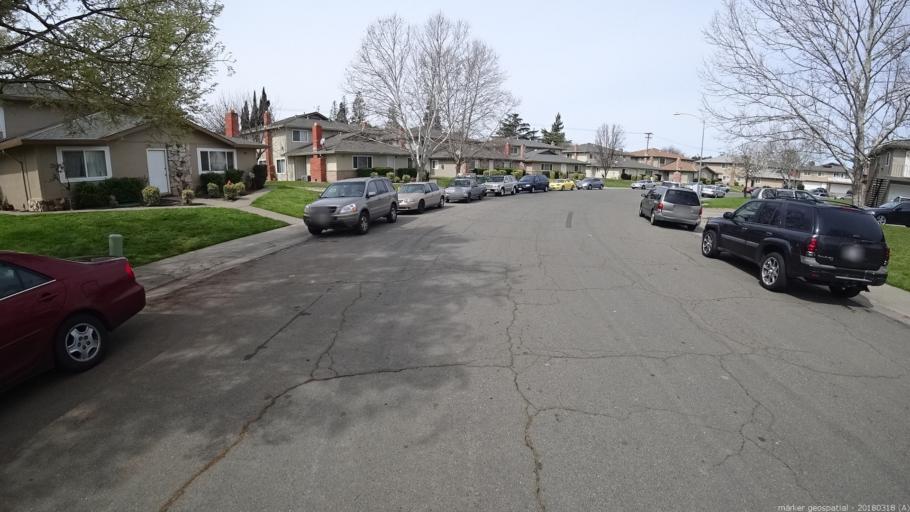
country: US
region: California
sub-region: Sacramento County
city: Parkway
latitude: 38.5236
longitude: -121.4590
